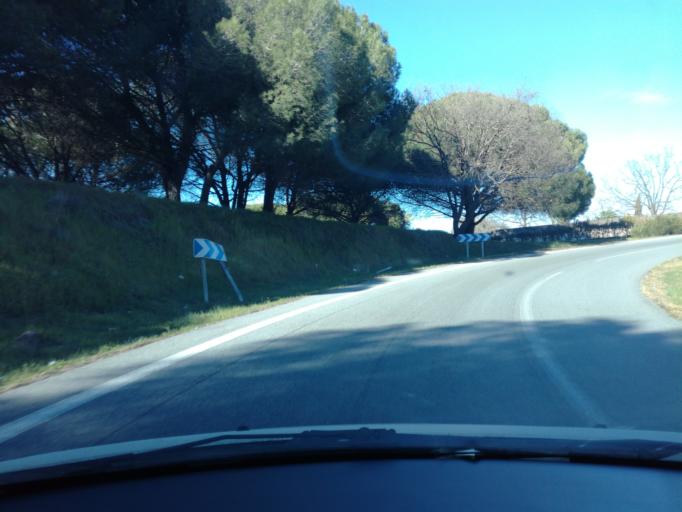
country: FR
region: Provence-Alpes-Cote d'Azur
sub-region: Departement du Var
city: Puget-sur-Argens
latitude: 43.4603
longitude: 6.6868
